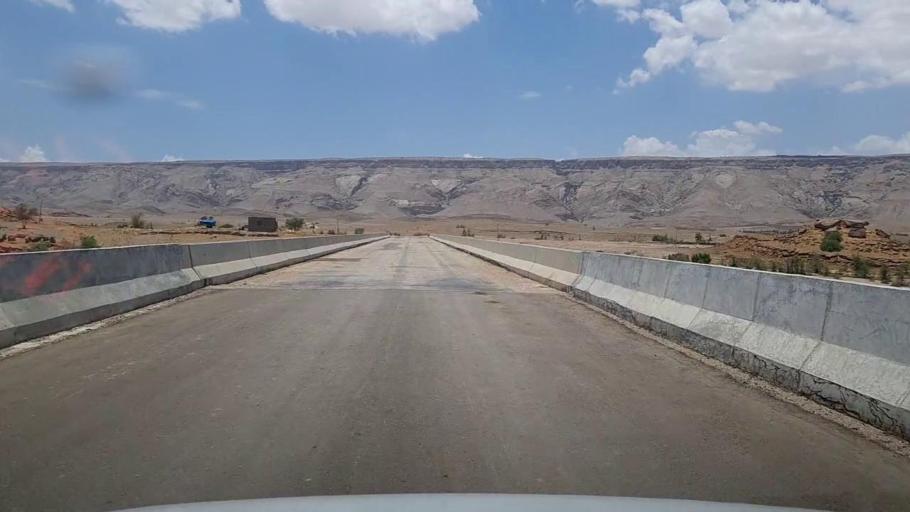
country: PK
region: Sindh
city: Bhan
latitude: 26.2668
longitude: 67.5193
